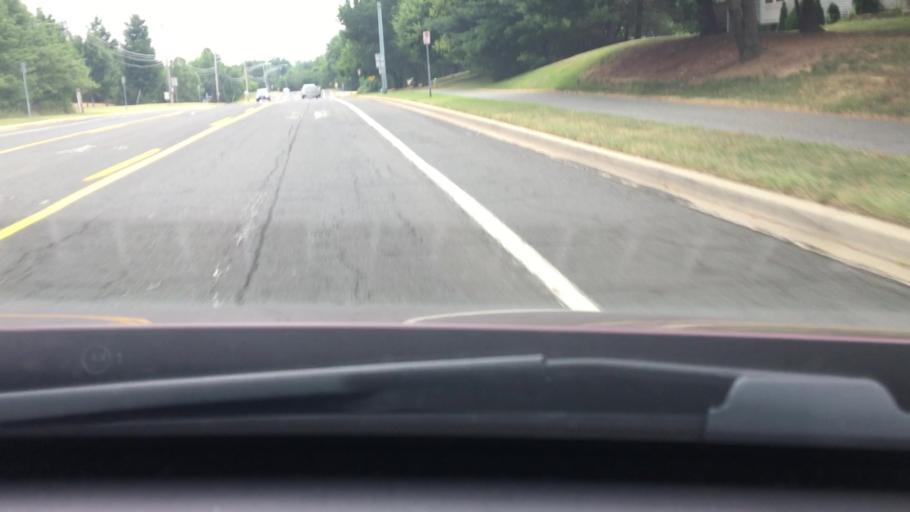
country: US
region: Maryland
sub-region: Montgomery County
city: Burtonsville
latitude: 39.0898
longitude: -76.9303
